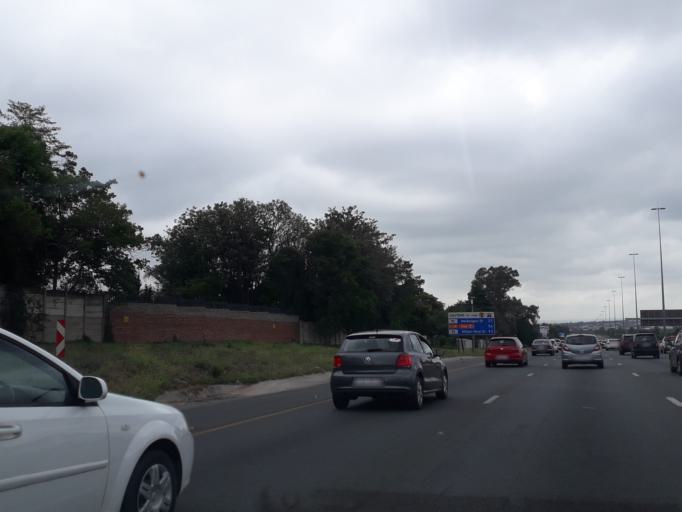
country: ZA
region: Gauteng
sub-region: City of Johannesburg Metropolitan Municipality
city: Roodepoort
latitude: -26.1067
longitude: 27.9600
